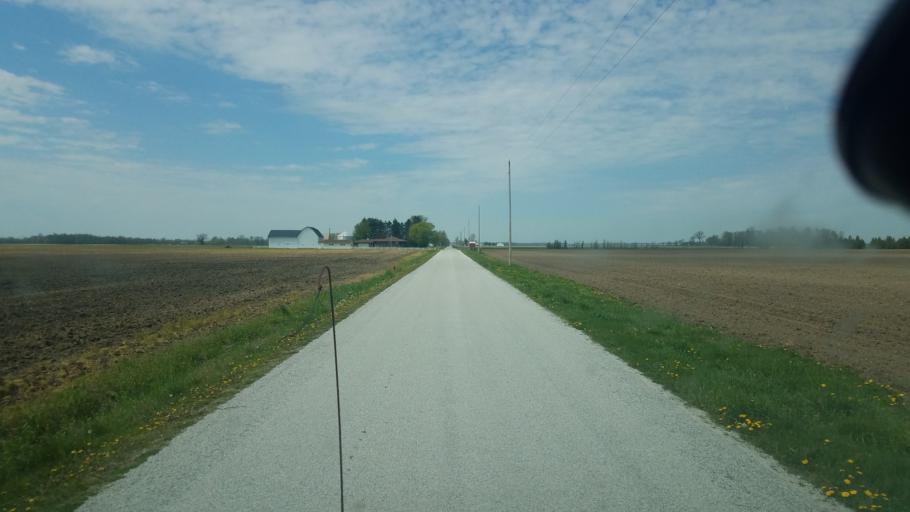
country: US
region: Ohio
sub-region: Hardin County
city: Kenton
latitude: 40.6584
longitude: -83.7380
